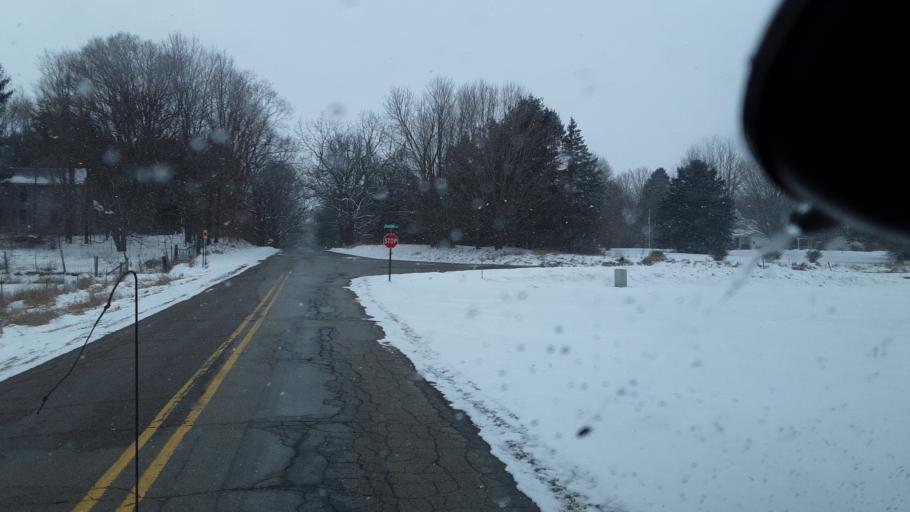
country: US
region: Michigan
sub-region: Ingham County
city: Leslie
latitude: 42.4910
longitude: -84.3884
